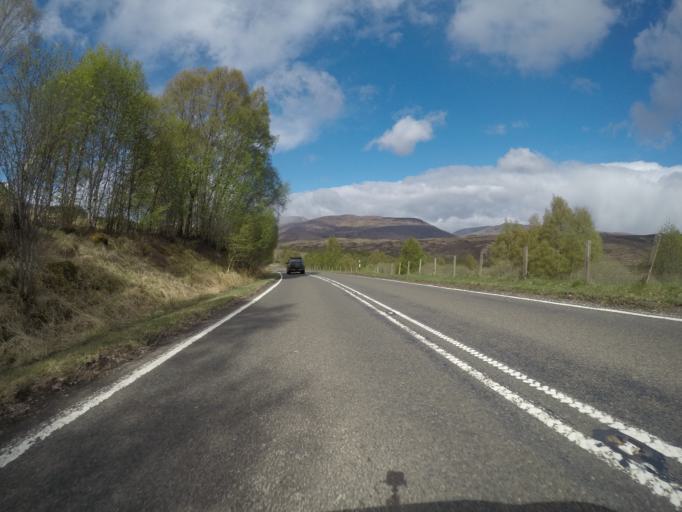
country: GB
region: Scotland
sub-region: Highland
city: Spean Bridge
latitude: 57.1420
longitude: -4.9529
